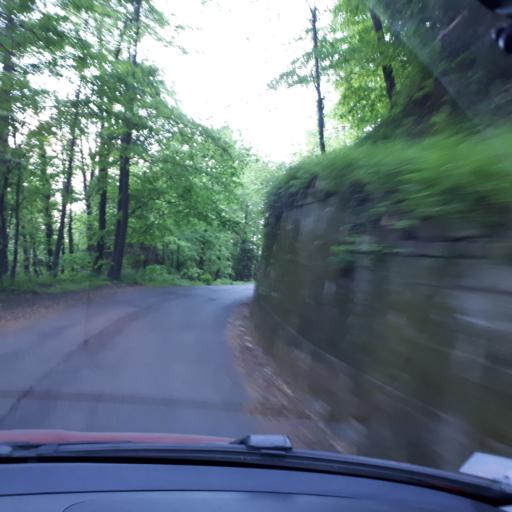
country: IT
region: Lombardy
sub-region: Provincia di Como
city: Musso
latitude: 46.1135
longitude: 9.2682
